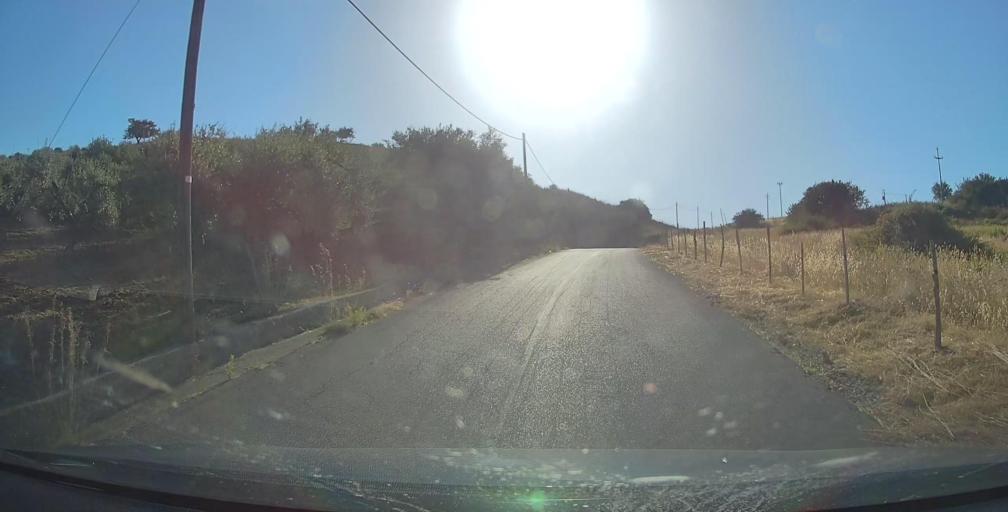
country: IT
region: Sicily
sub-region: Messina
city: San Piero Patti
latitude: 38.0759
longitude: 14.9808
